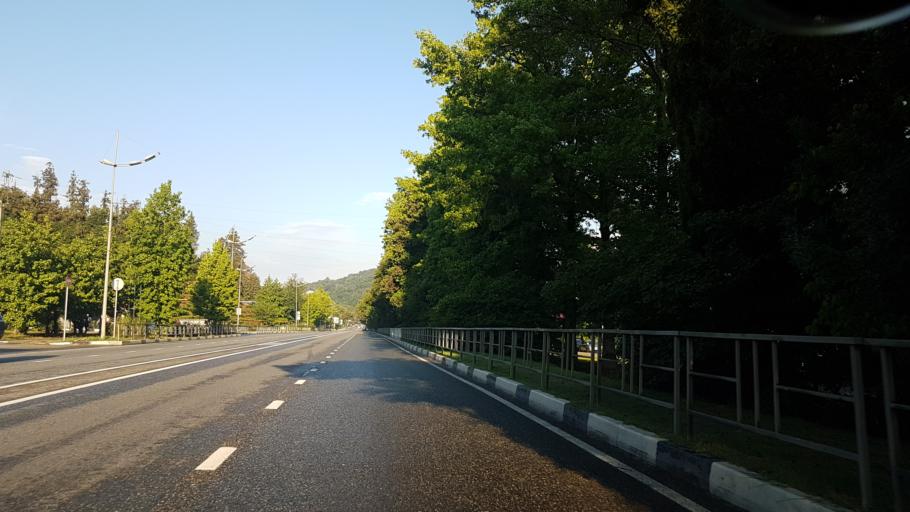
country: RU
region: Krasnodarskiy
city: Dagomys
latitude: 43.6619
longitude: 39.6685
